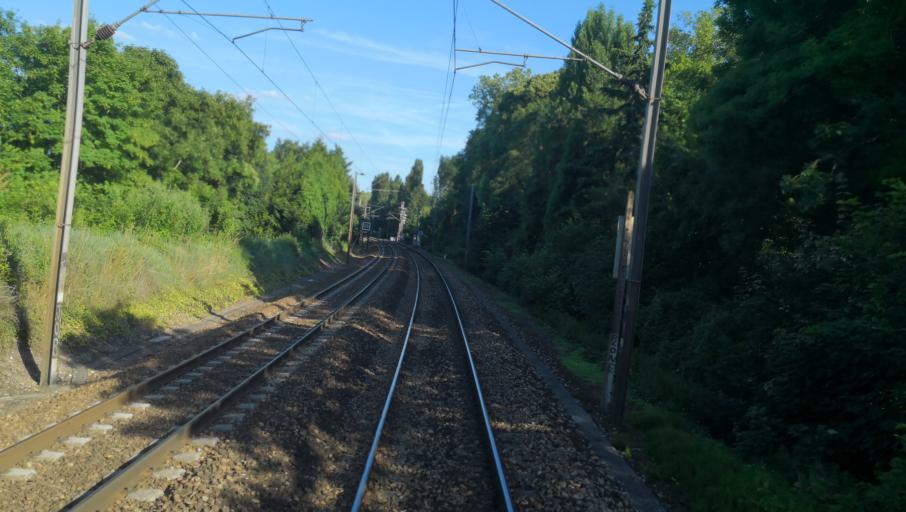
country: FR
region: Ile-de-France
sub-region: Departement des Yvelines
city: Villennes-sur-Seine
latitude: 48.9323
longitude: 2.0046
